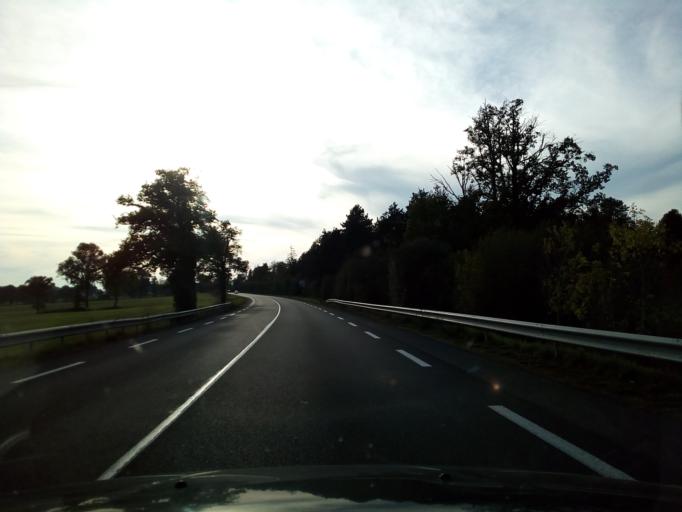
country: FR
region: Poitou-Charentes
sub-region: Departement de la Charente
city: Confolens
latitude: 45.9876
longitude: 0.6095
